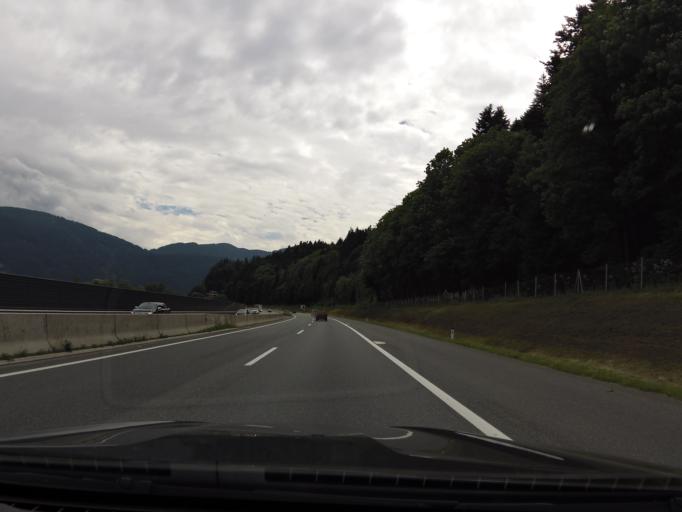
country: AT
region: Tyrol
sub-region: Politischer Bezirk Kufstein
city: Angath
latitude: 47.5060
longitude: 12.0596
